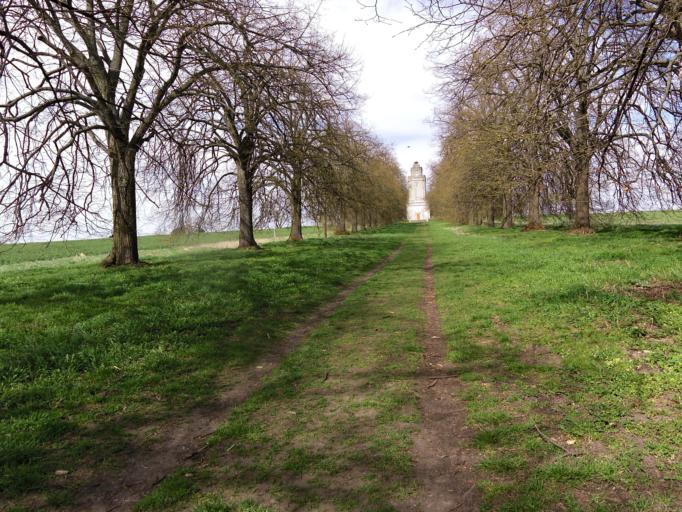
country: DE
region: Saxony
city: Schkeuditz
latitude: 51.3881
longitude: 12.2659
